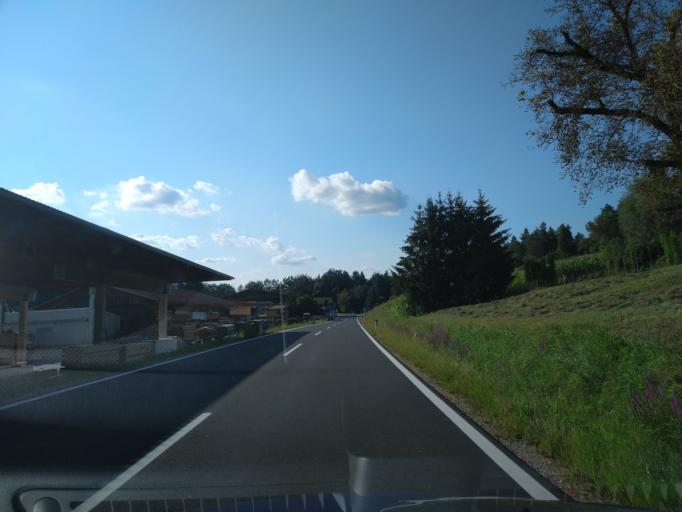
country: AT
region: Styria
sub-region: Politischer Bezirk Leibnitz
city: Gleinstatten
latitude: 46.7396
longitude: 15.3701
